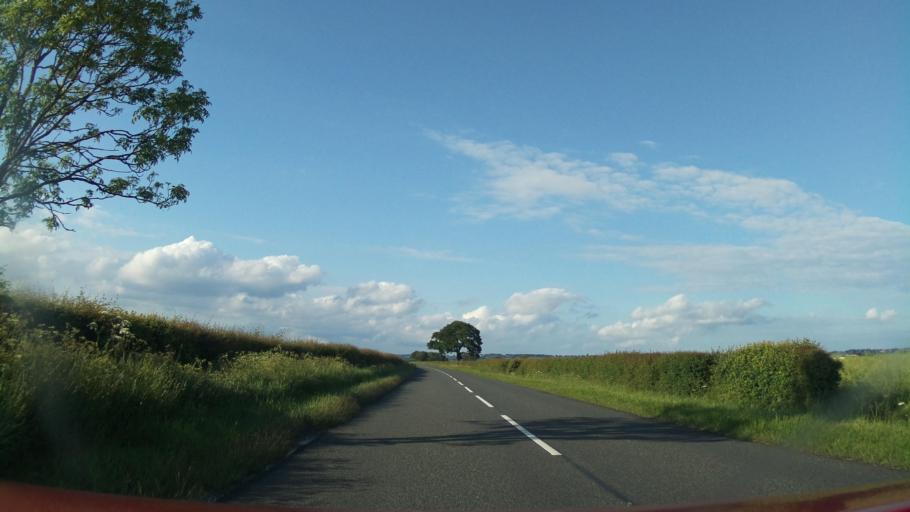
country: GB
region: England
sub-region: Lincolnshire
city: Navenby
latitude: 53.1047
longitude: -0.6068
